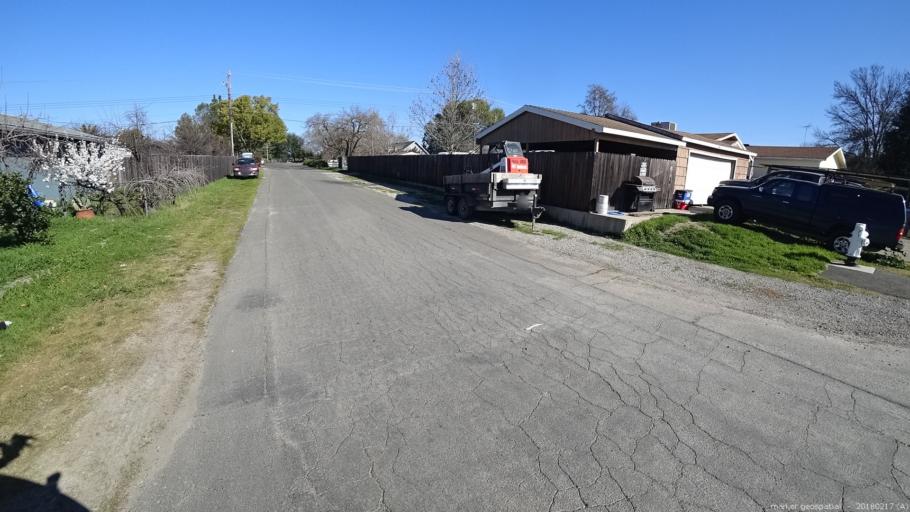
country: US
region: California
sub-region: Sacramento County
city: Orangevale
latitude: 38.7132
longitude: -121.2287
